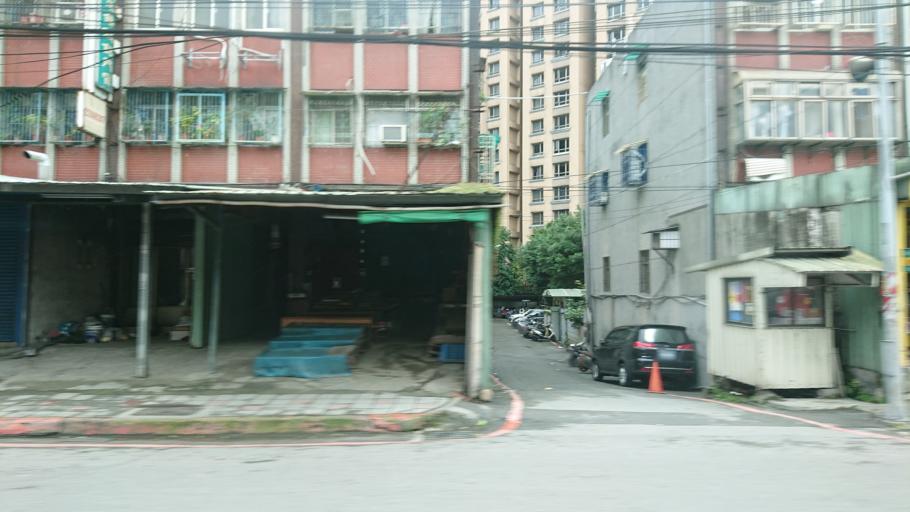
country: TW
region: Taipei
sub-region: Taipei
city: Banqiao
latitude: 24.9543
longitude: 121.4127
